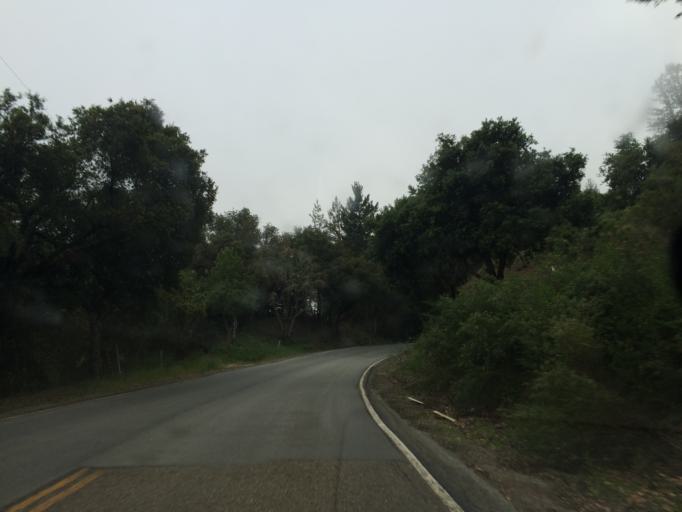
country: US
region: California
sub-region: Santa Clara County
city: Loyola
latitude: 37.3017
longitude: -122.1615
